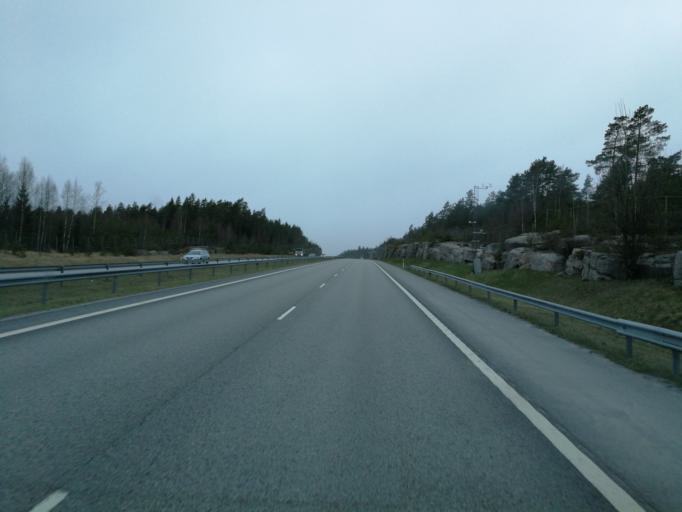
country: FI
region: Varsinais-Suomi
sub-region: Salo
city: Halikko
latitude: 60.4350
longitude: 22.9700
